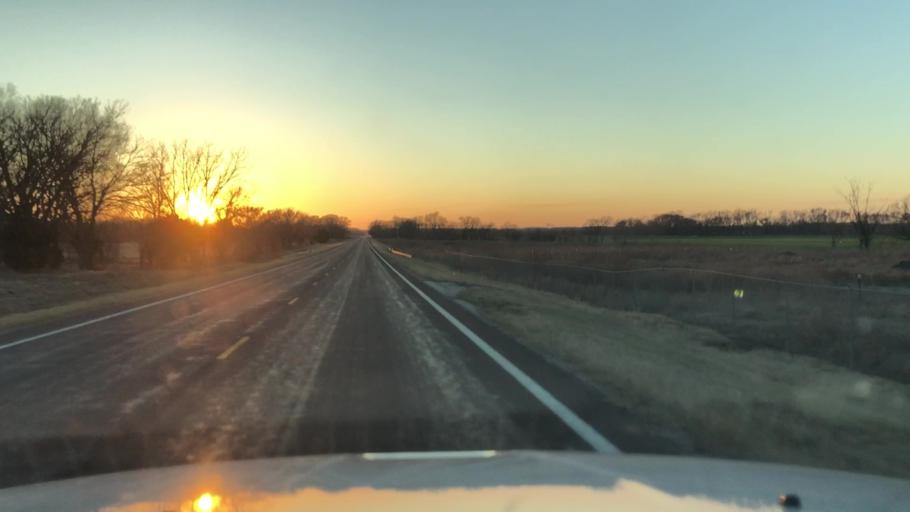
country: US
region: Kansas
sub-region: Montgomery County
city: Caney
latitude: 37.0674
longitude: -95.9501
